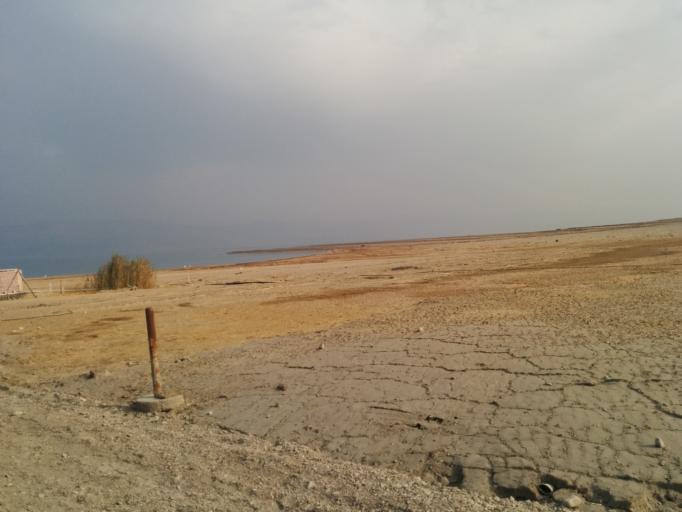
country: PS
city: `Arab ar Rashaydah
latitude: 31.4207
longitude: 35.3899
